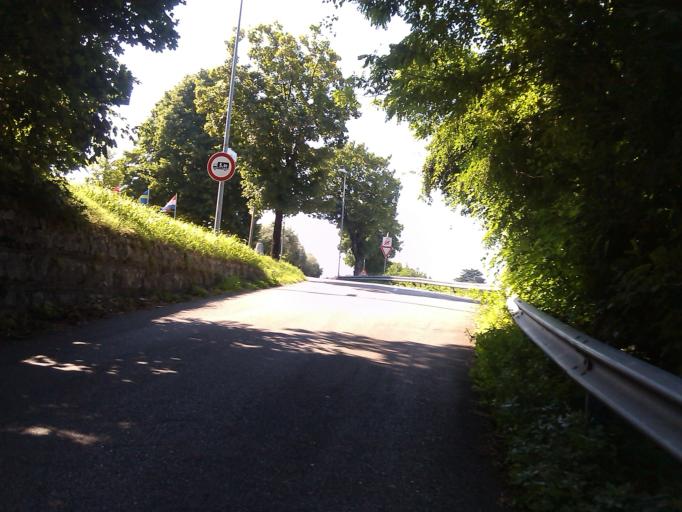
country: IT
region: Veneto
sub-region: Provincia di Vicenza
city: Bassano del Grappa
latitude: 45.7795
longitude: 11.7412
